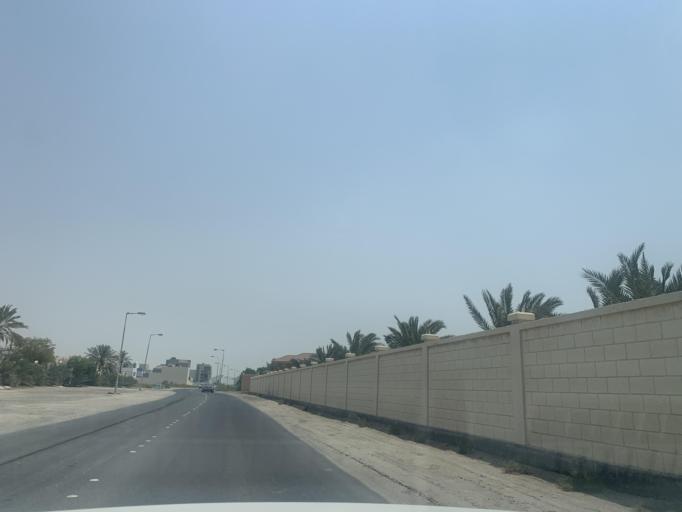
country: BH
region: Central Governorate
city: Madinat Hamad
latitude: 26.1376
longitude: 50.4621
